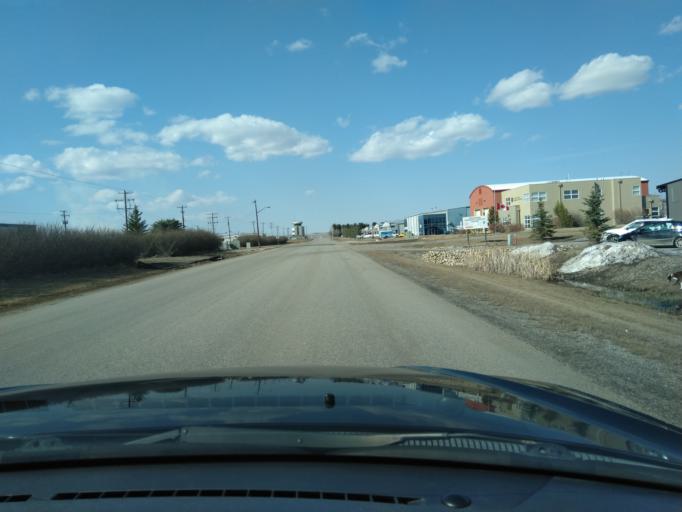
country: CA
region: Alberta
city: Cochrane
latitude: 51.0973
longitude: -114.3738
